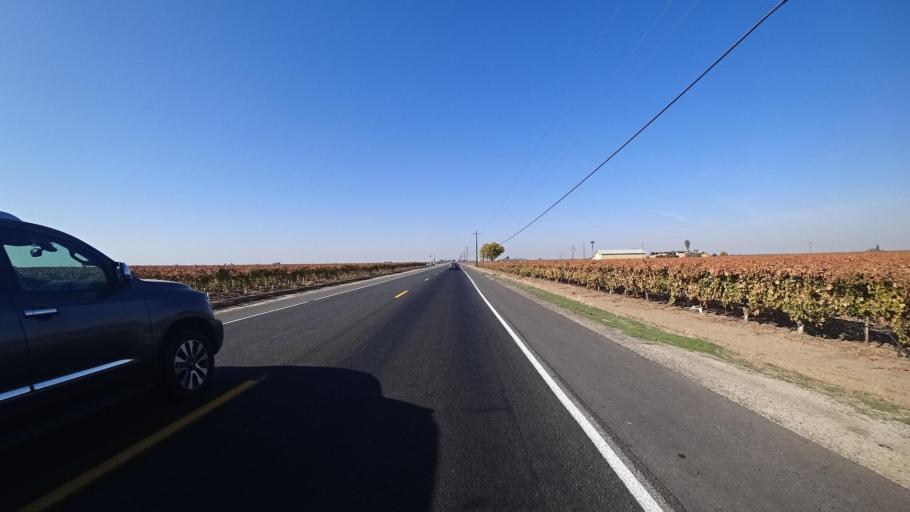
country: US
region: California
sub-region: Kern County
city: Delano
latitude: 35.7178
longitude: -119.2918
